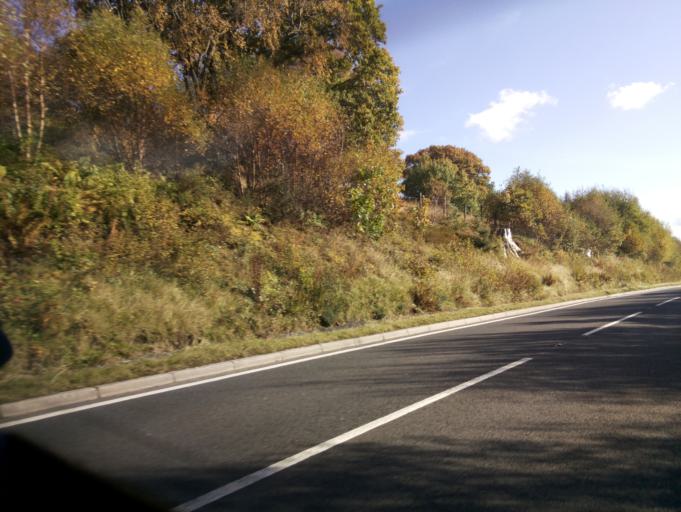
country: GB
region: Wales
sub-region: Rhondda Cynon Taf
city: Hirwaun
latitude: 51.8308
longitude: -3.4584
